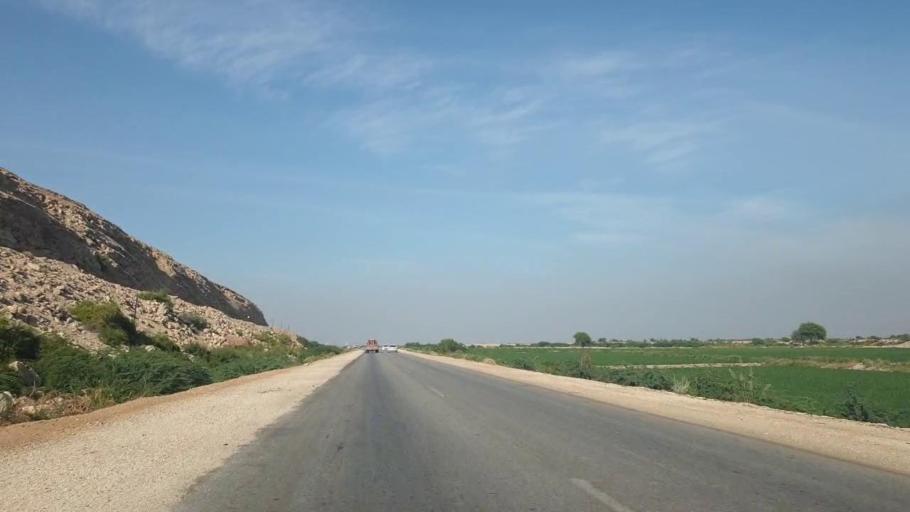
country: PK
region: Sindh
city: Sehwan
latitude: 26.3594
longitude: 67.8733
